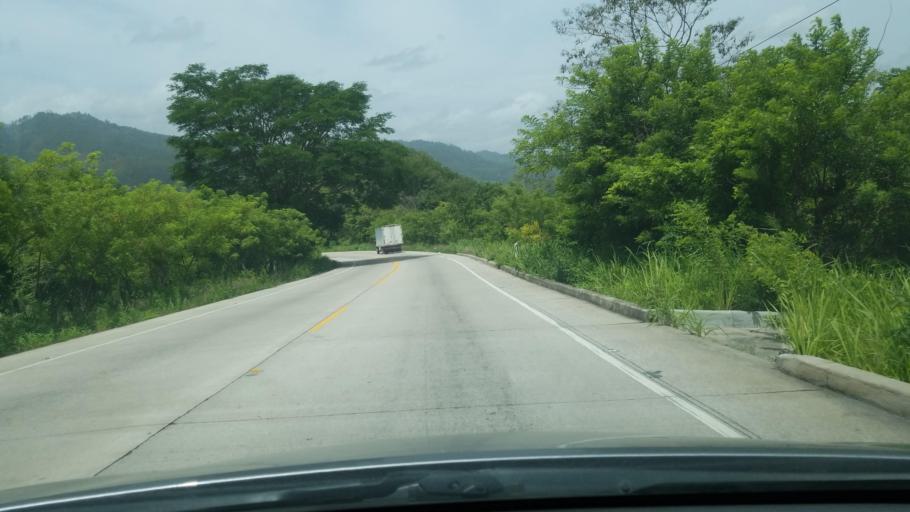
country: HN
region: Copan
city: Quezailica
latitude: 14.9049
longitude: -88.7545
